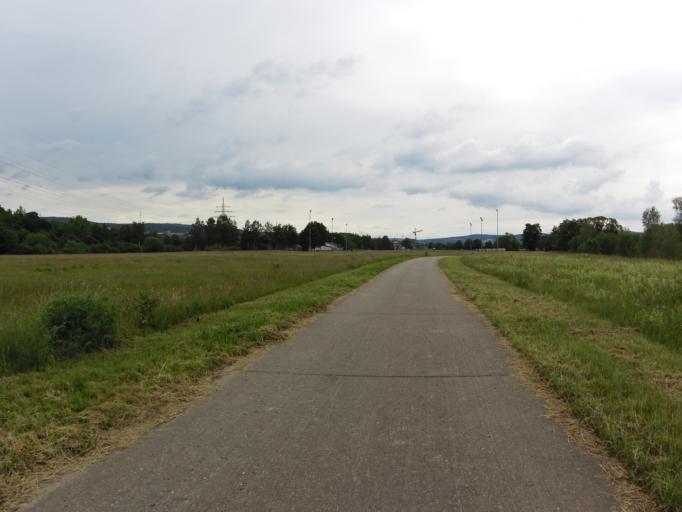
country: DE
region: Hesse
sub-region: Regierungsbezirk Kassel
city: Bad Hersfeld
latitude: 50.8701
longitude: 9.7267
